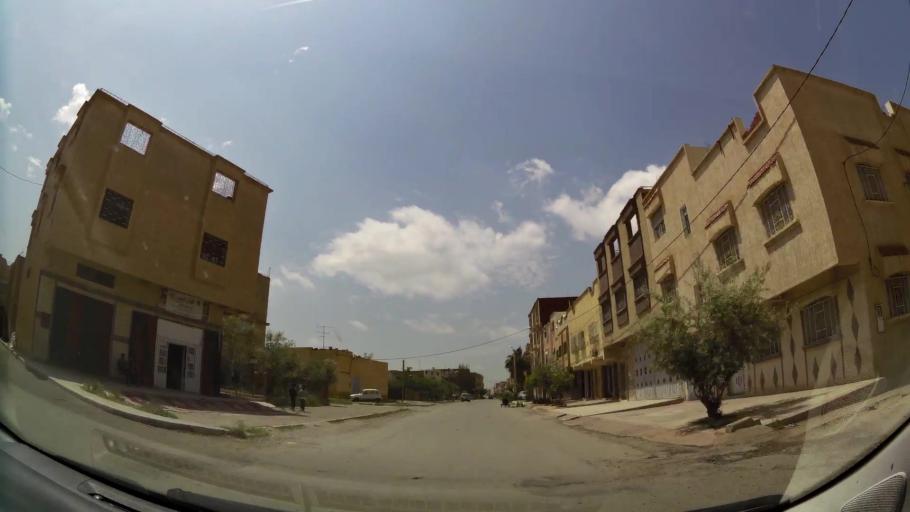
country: MA
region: Oriental
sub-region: Oujda-Angad
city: Oujda
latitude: 34.6878
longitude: -1.8869
